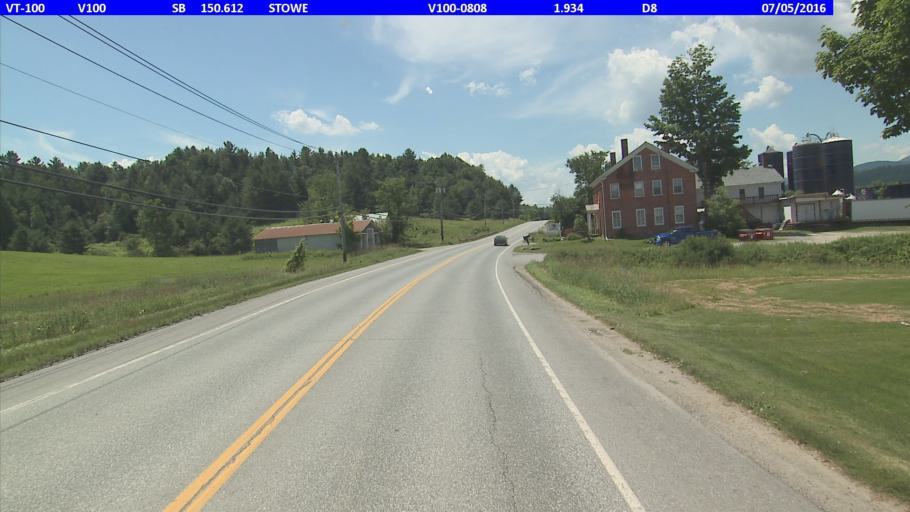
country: US
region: Vermont
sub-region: Washington County
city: Waterbury
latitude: 44.4483
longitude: -72.6998
